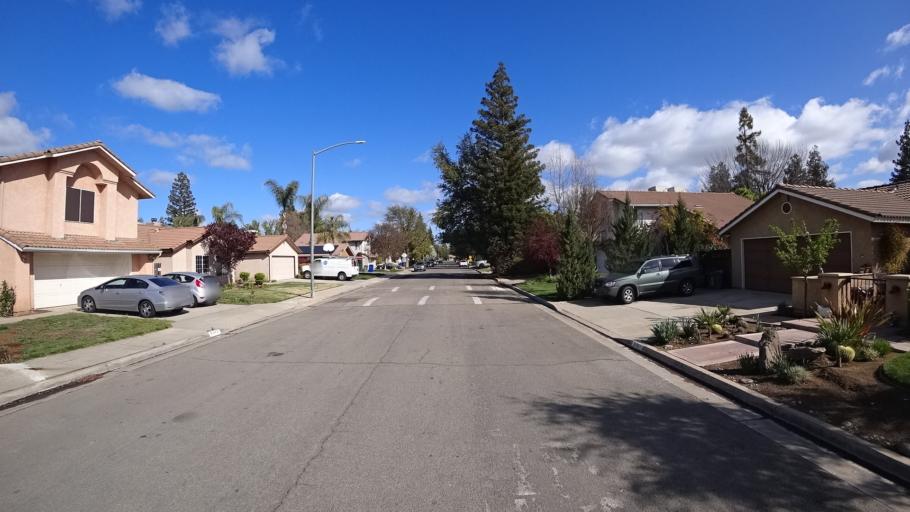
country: US
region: California
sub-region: Fresno County
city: West Park
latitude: 36.8273
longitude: -119.8824
